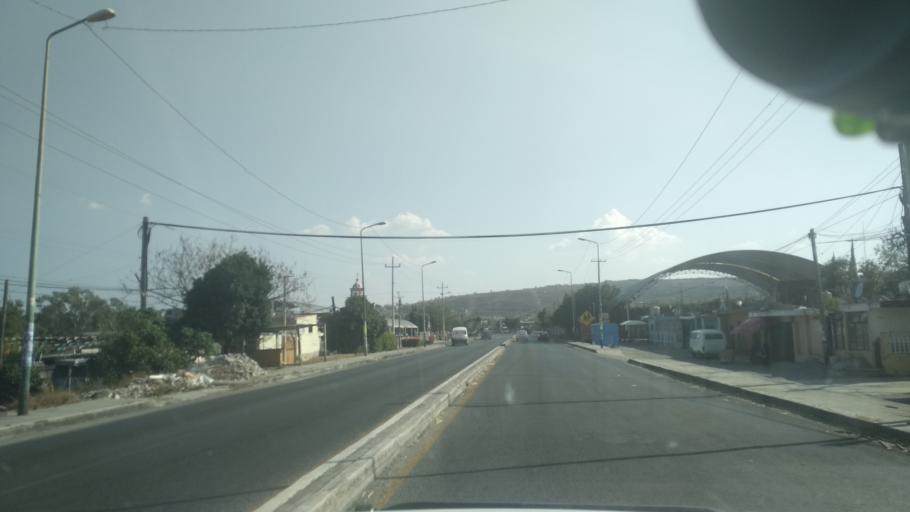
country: MX
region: Puebla
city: Izucar de Matamoros
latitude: 18.6242
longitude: -98.4702
